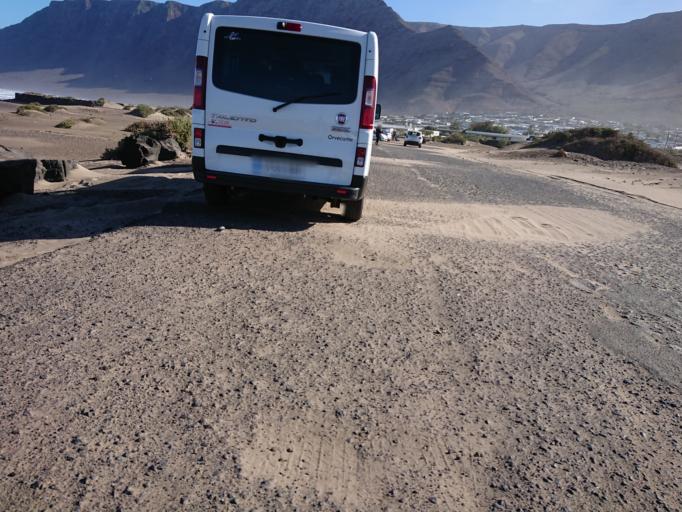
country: ES
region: Canary Islands
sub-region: Provincia de Las Palmas
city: Teguise
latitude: 29.1152
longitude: -13.5541
